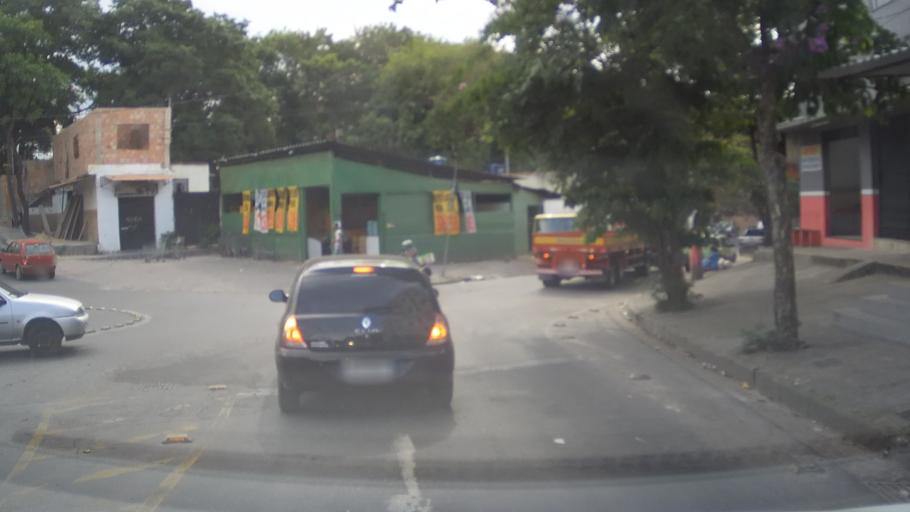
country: BR
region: Minas Gerais
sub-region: Belo Horizonte
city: Belo Horizonte
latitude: -19.8659
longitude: -43.9034
